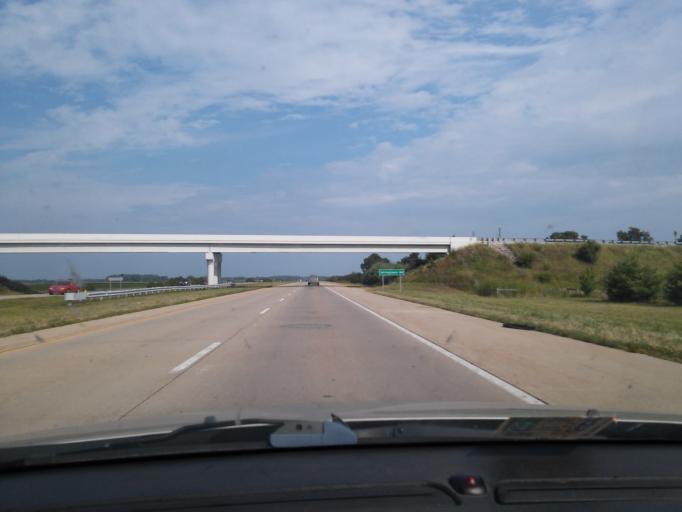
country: US
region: Ohio
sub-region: Greene County
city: Wilberforce
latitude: 39.6852
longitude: -83.8473
